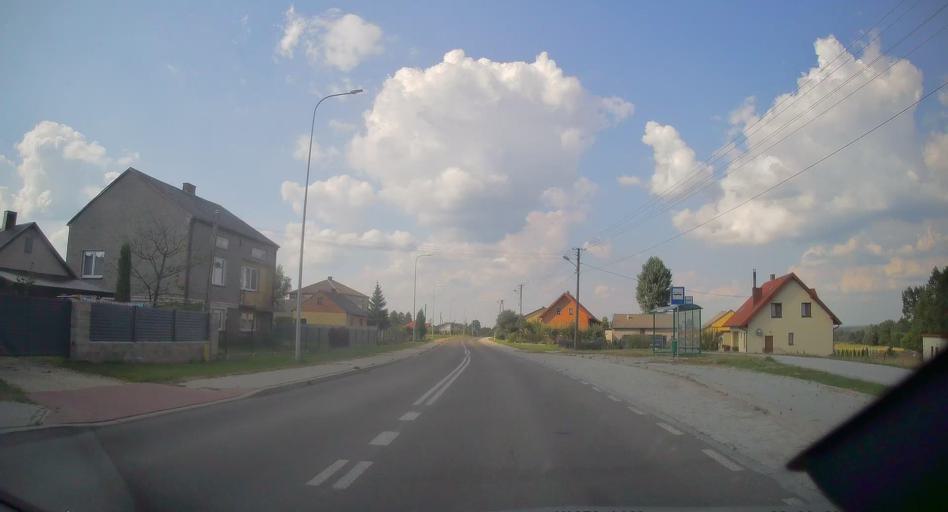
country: PL
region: Swietokrzyskie
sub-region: Powiat konecki
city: Radoszyce
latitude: 51.0270
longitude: 20.2904
